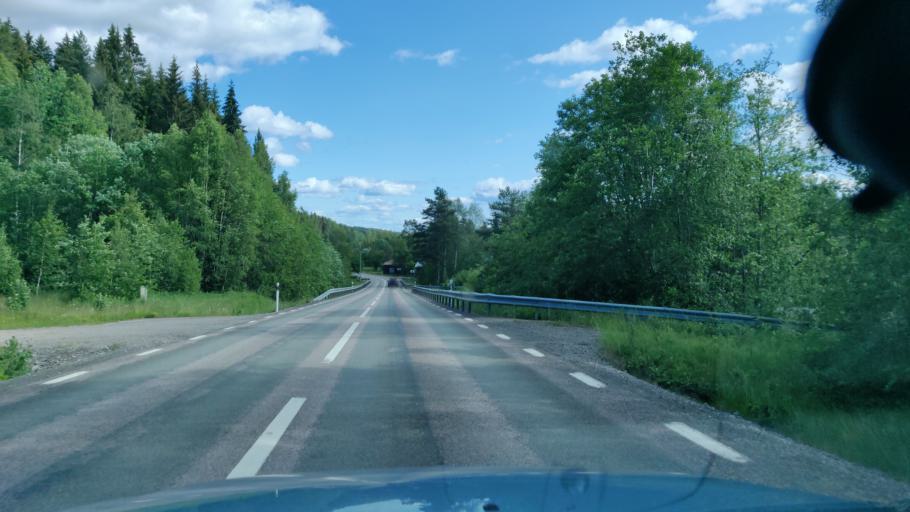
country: SE
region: Vaermland
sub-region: Torsby Kommun
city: Torsby
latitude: 60.5646
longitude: 13.0940
